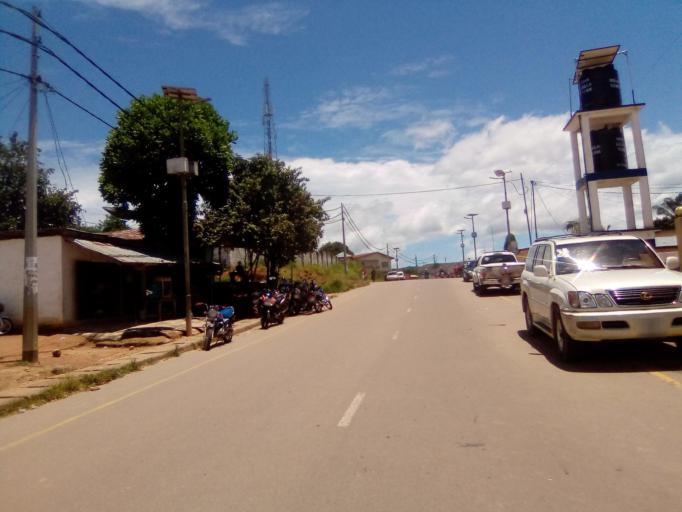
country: SL
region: Eastern Province
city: Koidu
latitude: 8.6397
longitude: -10.9756
